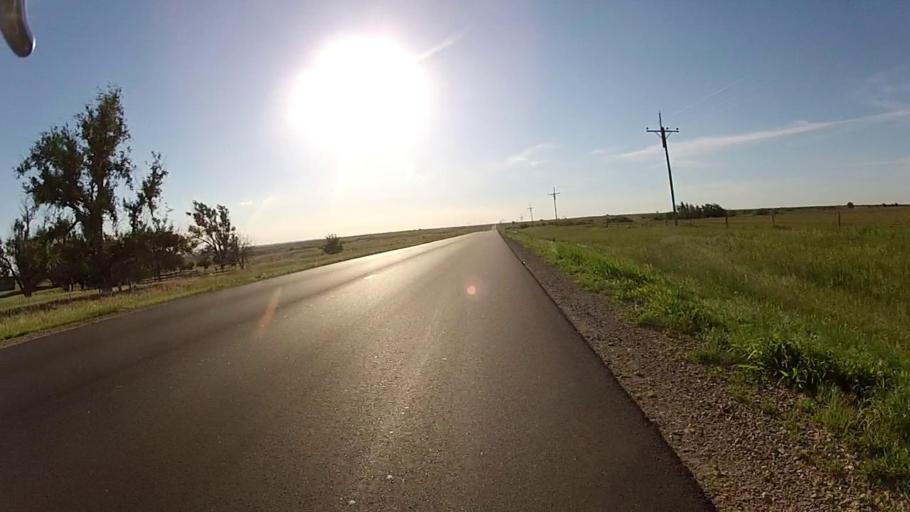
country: US
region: Kansas
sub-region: Comanche County
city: Coldwater
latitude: 37.2821
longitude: -99.1346
